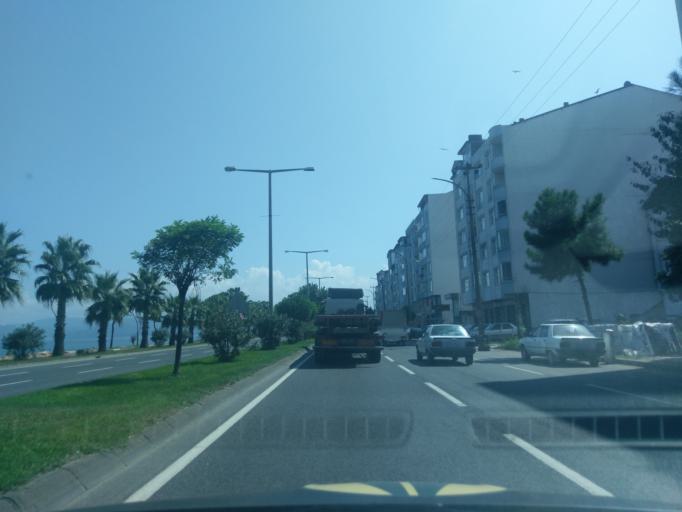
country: TR
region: Ordu
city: Fatsa
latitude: 41.0265
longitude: 37.5144
